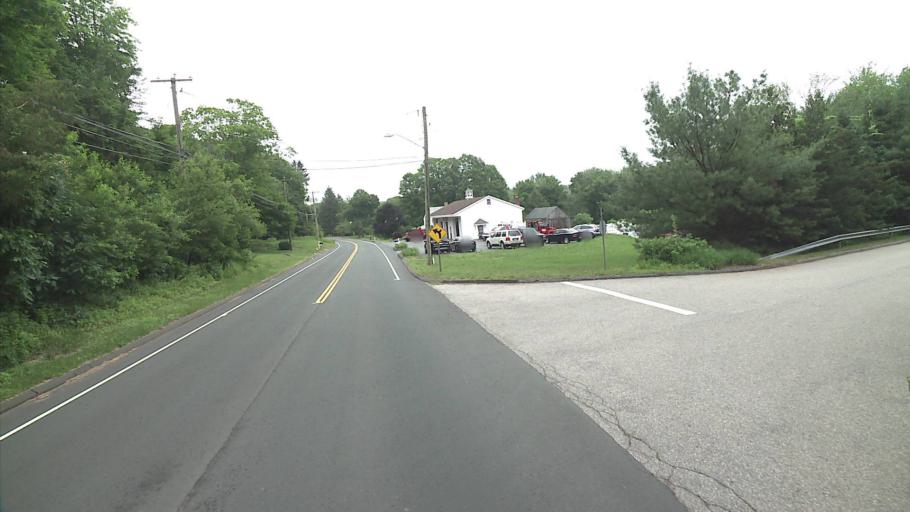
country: US
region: Connecticut
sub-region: Hartford County
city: Manchester
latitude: 41.7102
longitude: -72.5167
